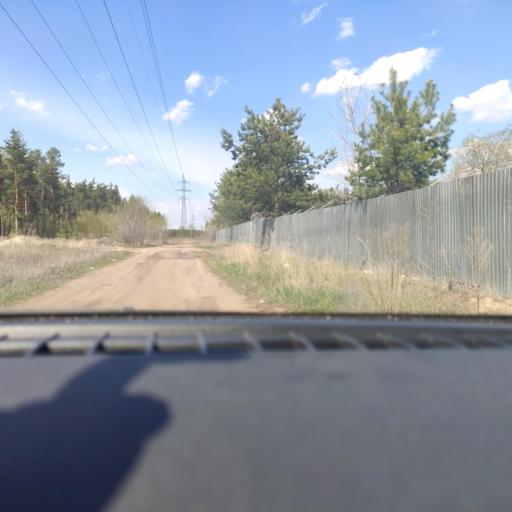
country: RU
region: Voronezj
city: Maslovka
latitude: 51.5943
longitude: 39.2158
